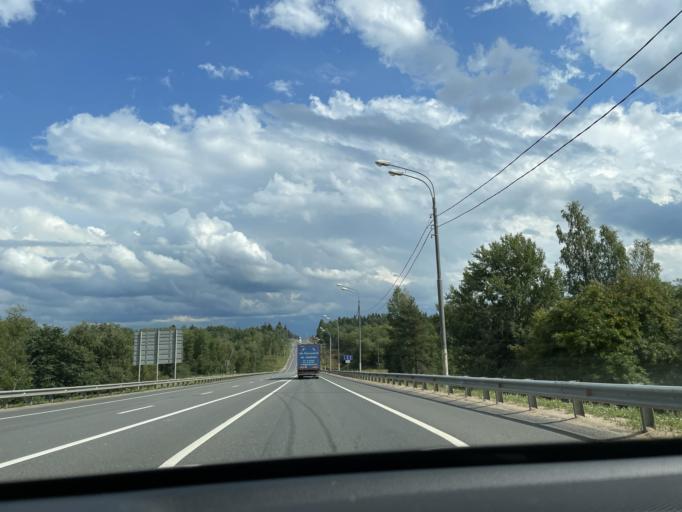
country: RU
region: Novgorod
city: Valday
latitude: 57.9514
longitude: 33.2948
